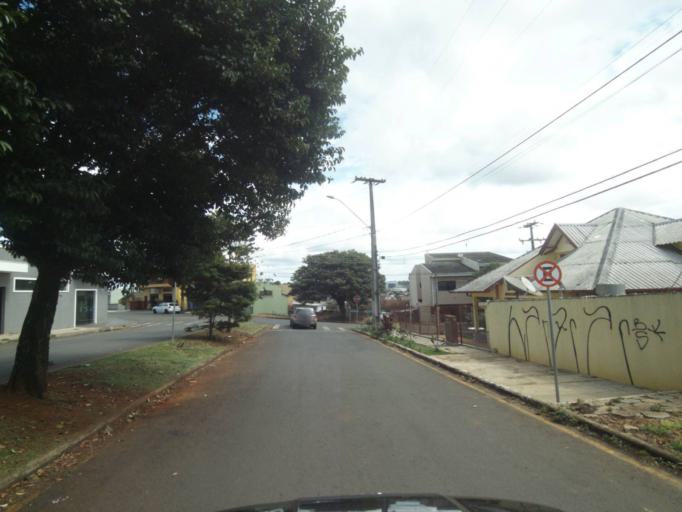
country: BR
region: Parana
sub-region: Telemaco Borba
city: Telemaco Borba
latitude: -24.3228
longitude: -50.6343
